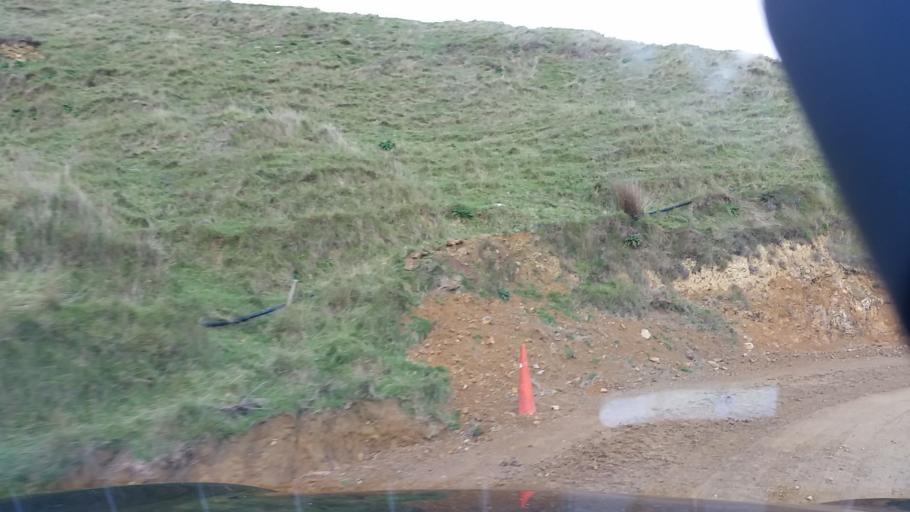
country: NZ
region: Marlborough
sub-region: Marlborough District
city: Picton
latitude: -40.9864
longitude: 173.8311
